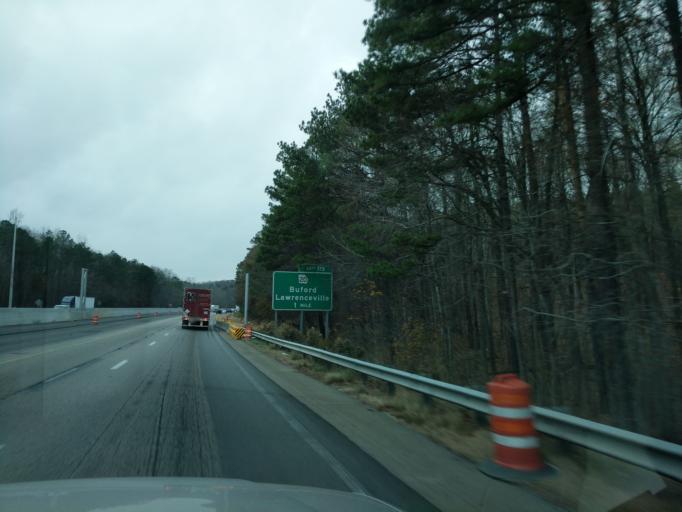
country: US
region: Georgia
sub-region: Gwinnett County
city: Buford
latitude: 34.0569
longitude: -83.9681
